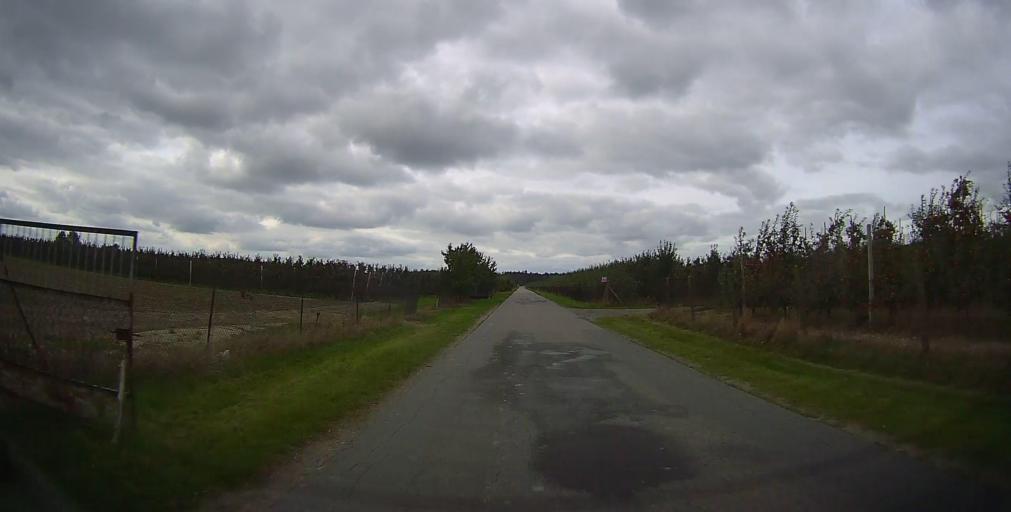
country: PL
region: Masovian Voivodeship
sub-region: Powiat grojecki
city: Goszczyn
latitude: 51.7677
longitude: 20.8674
